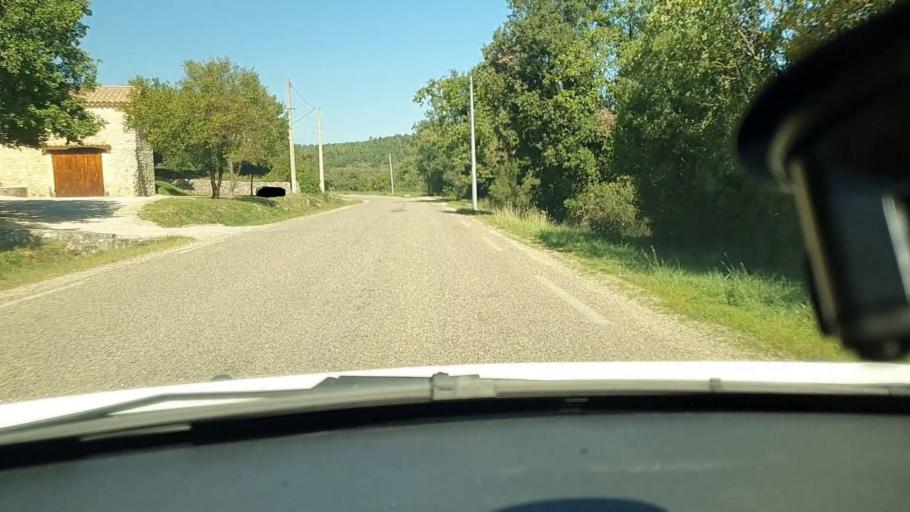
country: FR
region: Languedoc-Roussillon
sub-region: Departement du Gard
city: Goudargues
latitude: 44.1567
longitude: 4.4585
